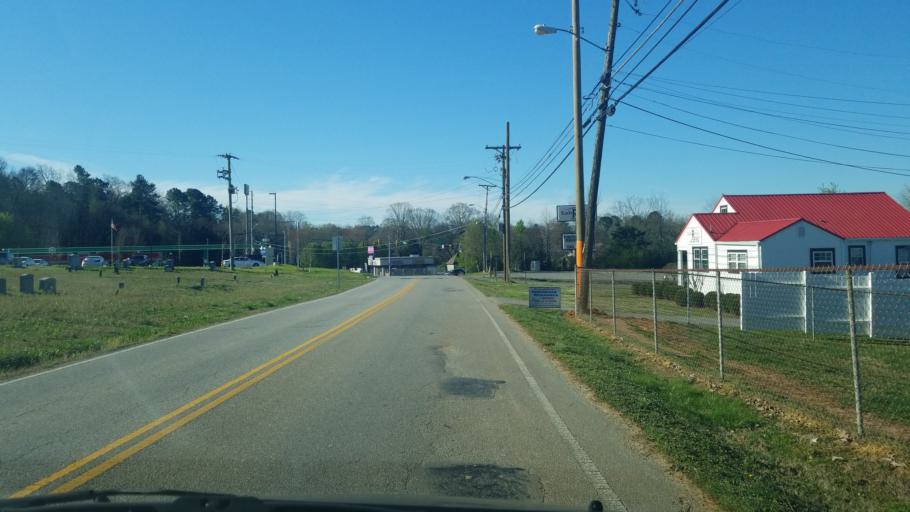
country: US
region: Tennessee
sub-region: Hamilton County
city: East Brainerd
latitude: 35.0192
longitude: -85.1734
